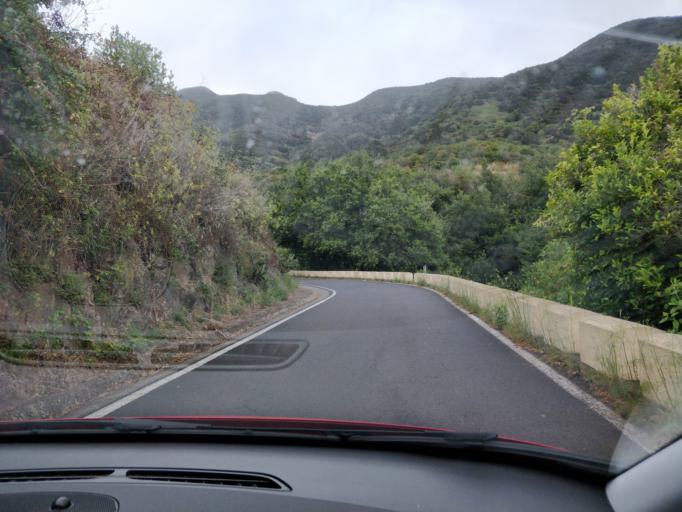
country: ES
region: Canary Islands
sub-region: Provincia de Santa Cruz de Tenerife
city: Santiago del Teide
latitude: 28.3242
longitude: -16.8428
